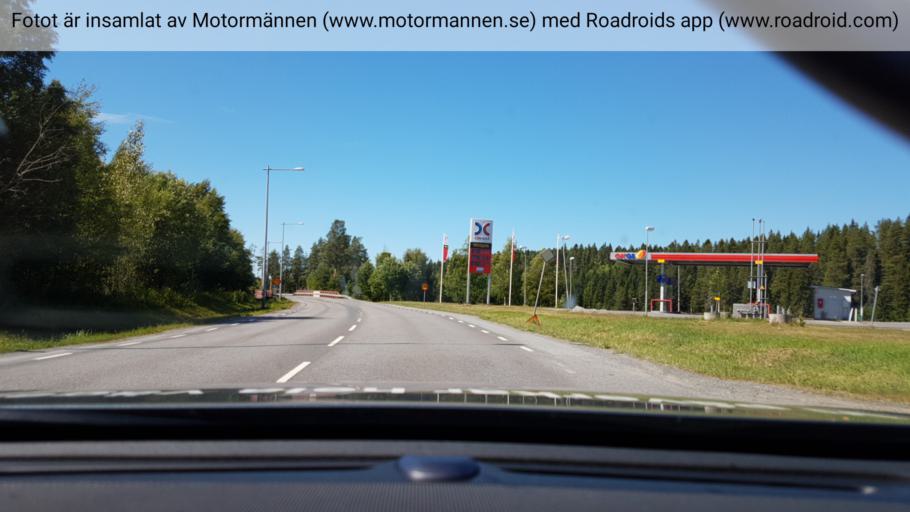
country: SE
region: Vaesterbotten
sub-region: Skelleftea Kommun
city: Skelleftea
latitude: 64.7619
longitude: 20.9488
